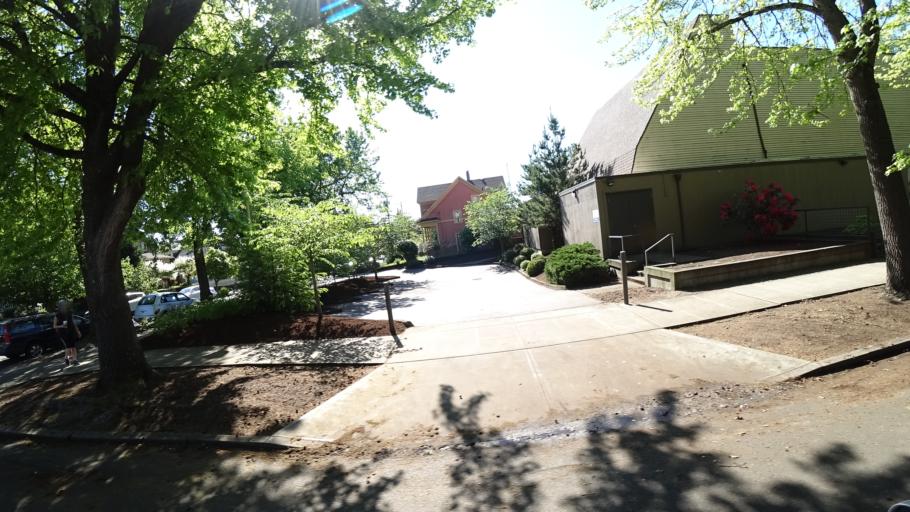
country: US
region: Oregon
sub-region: Multnomah County
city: Portland
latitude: 45.5252
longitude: -122.6359
